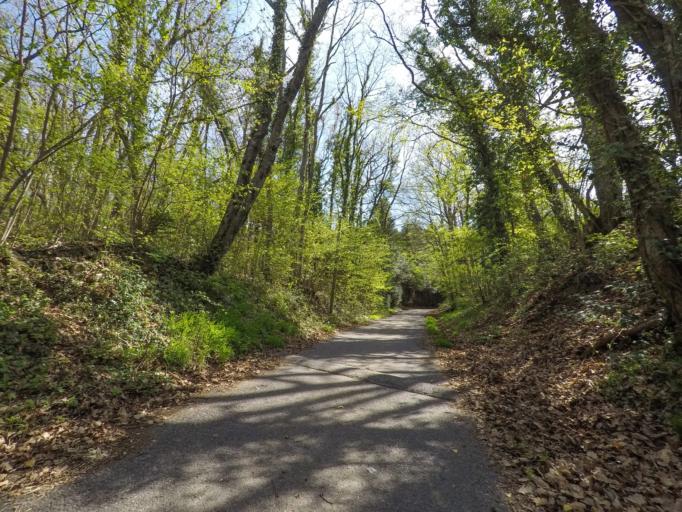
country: FR
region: Rhone-Alpes
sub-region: Departement de la Haute-Savoie
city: Collonges-sous-Saleve
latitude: 46.1270
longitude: 6.1534
